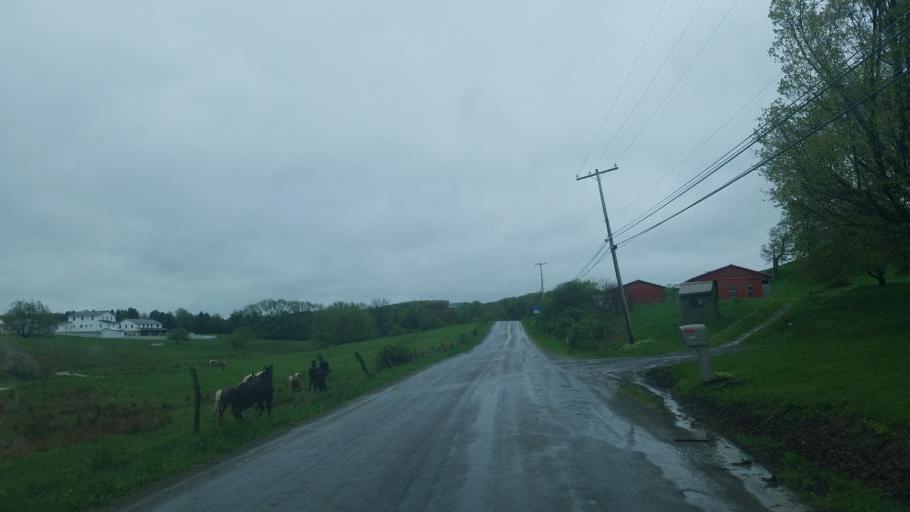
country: US
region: Pennsylvania
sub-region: Potter County
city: Galeton
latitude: 41.9115
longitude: -77.7750
